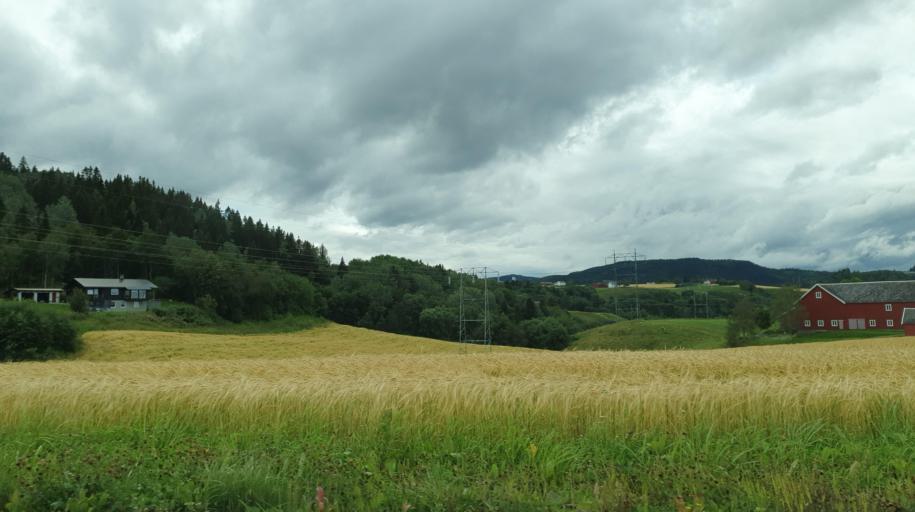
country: NO
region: Nord-Trondelag
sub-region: Stjordal
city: Stjordalshalsen
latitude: 63.4334
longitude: 10.9519
